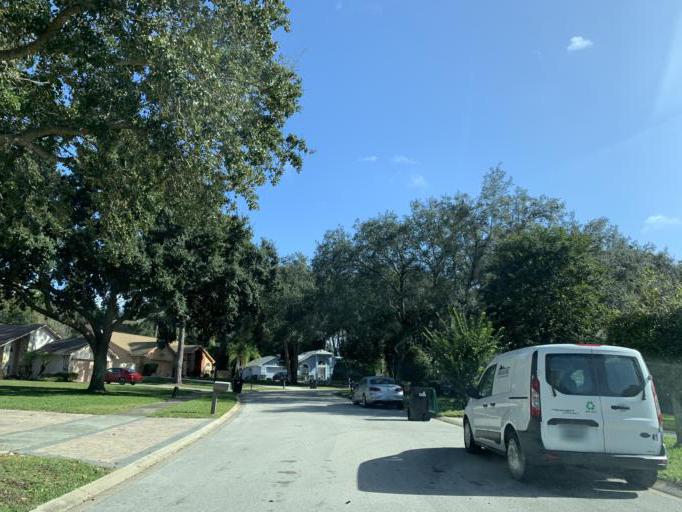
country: US
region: Florida
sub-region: Orange County
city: Clarcona
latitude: 28.6322
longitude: -81.4734
